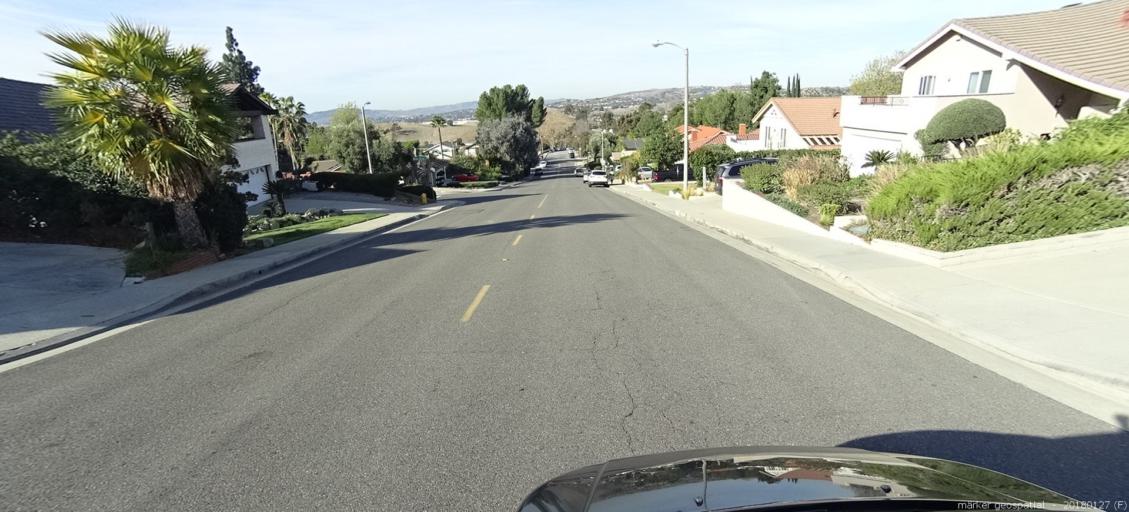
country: US
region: California
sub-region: Los Angeles County
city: Diamond Bar
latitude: 34.0360
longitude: -117.8004
